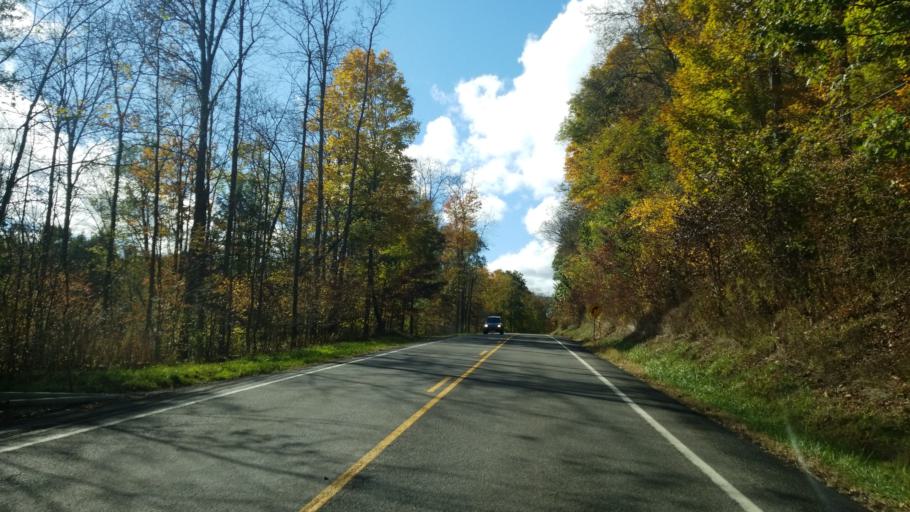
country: US
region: Pennsylvania
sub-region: Jefferson County
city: Sykesville
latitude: 41.0916
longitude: -78.8295
